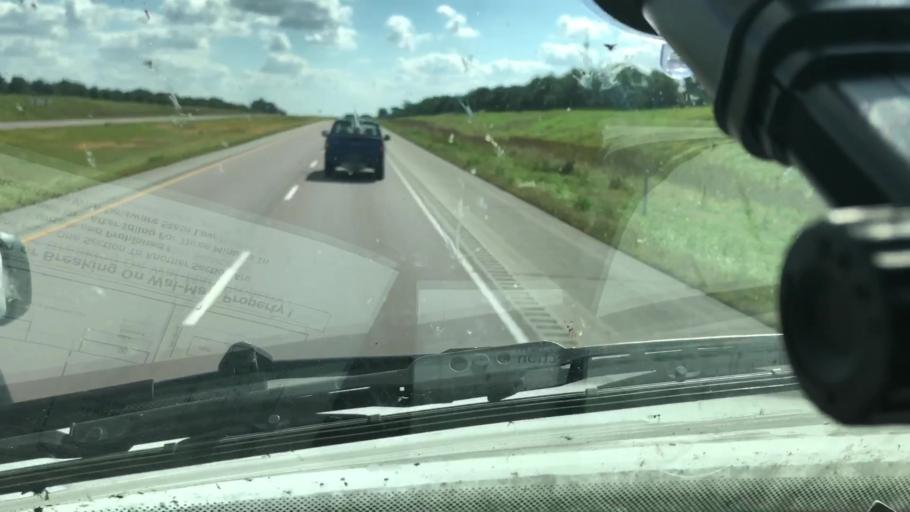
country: US
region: Iowa
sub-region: Worth County
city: Manly
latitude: 43.2990
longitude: -93.3498
